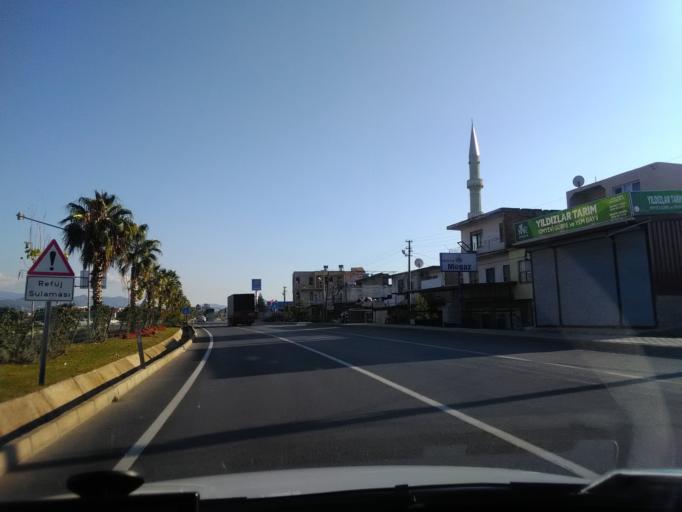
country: TR
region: Antalya
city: Gazipasa
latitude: 36.2938
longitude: 32.2878
